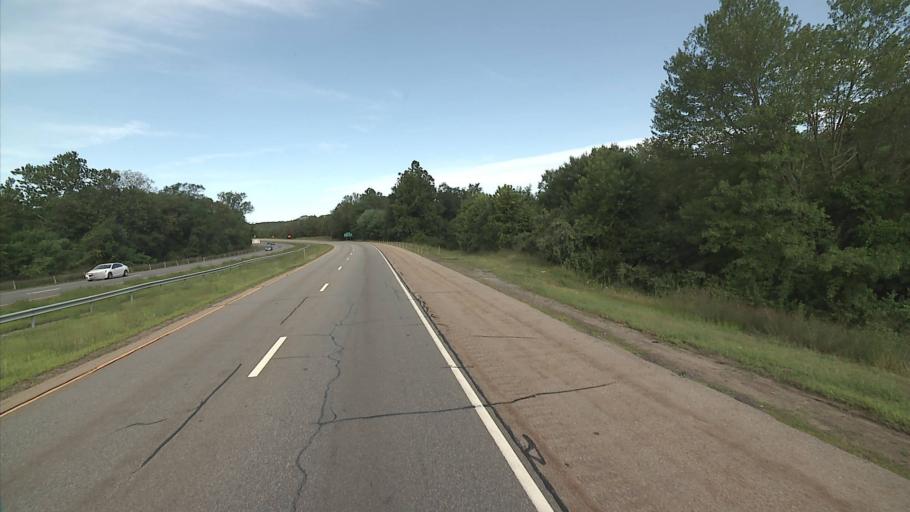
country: US
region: Connecticut
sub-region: New London County
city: Norwich
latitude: 41.5650
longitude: -72.1350
